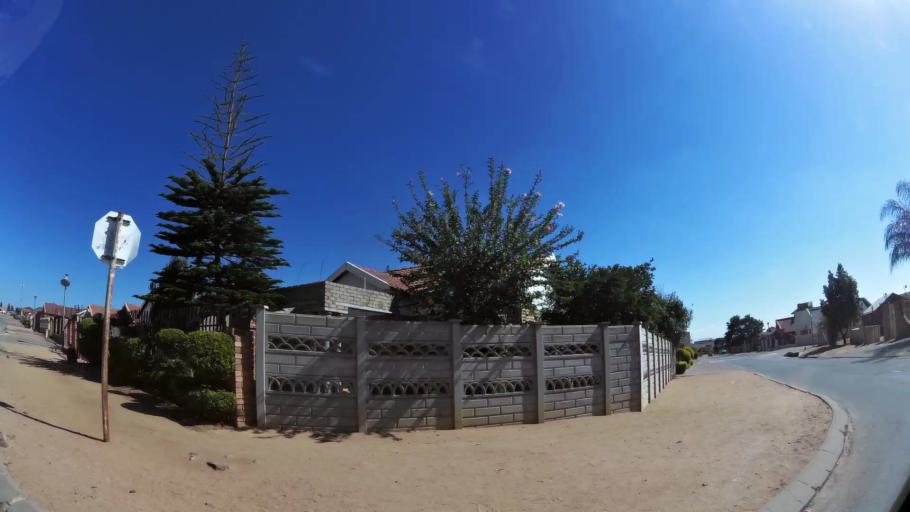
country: ZA
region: Limpopo
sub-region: Capricorn District Municipality
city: Polokwane
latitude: -23.8732
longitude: 29.4137
